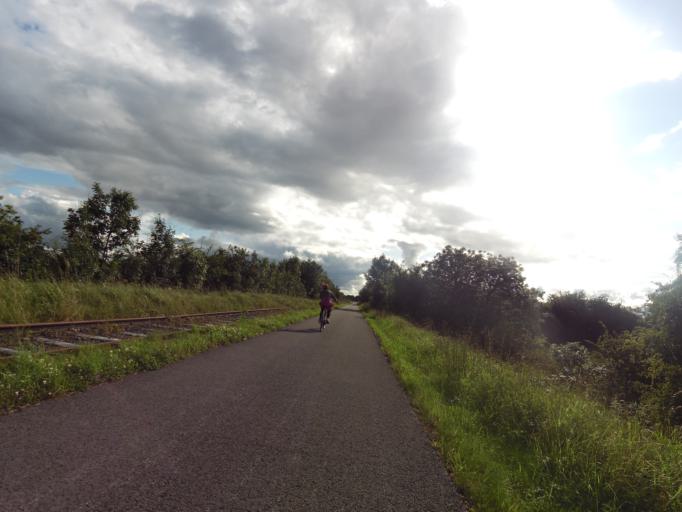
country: IE
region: Leinster
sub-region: An Iarmhi
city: Kilbeggan
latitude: 53.4727
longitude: -7.4883
